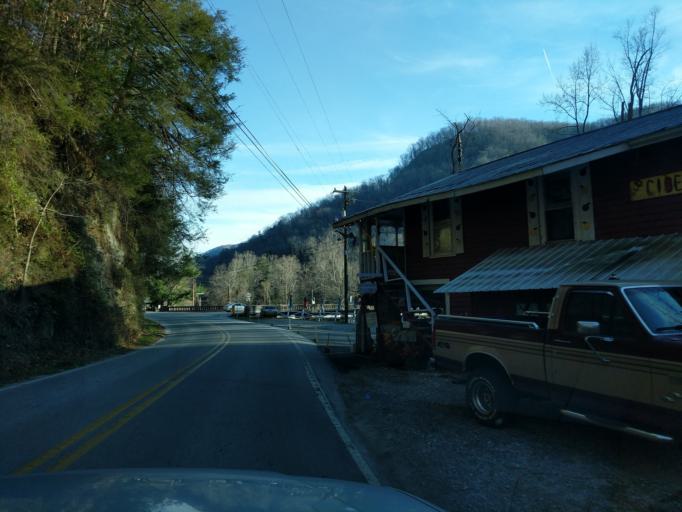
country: US
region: North Carolina
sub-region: Henderson County
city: Edneyville
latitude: 35.4519
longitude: -82.2878
